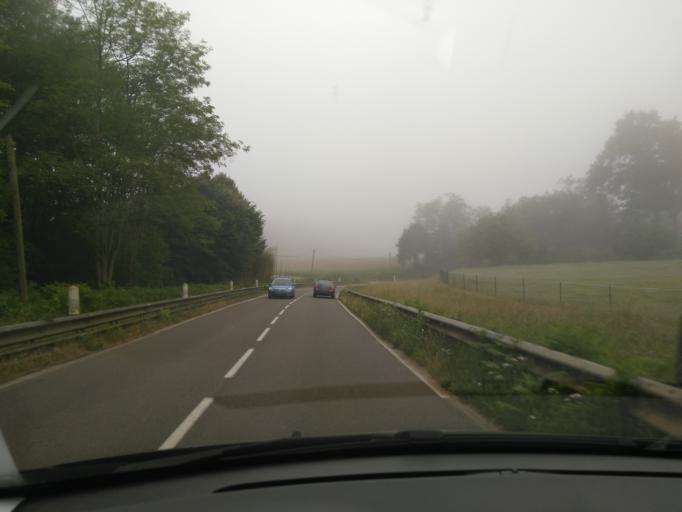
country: FR
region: Aquitaine
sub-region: Departement des Landes
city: Villeneuve-de-Marsan
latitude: 43.8860
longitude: -0.3825
